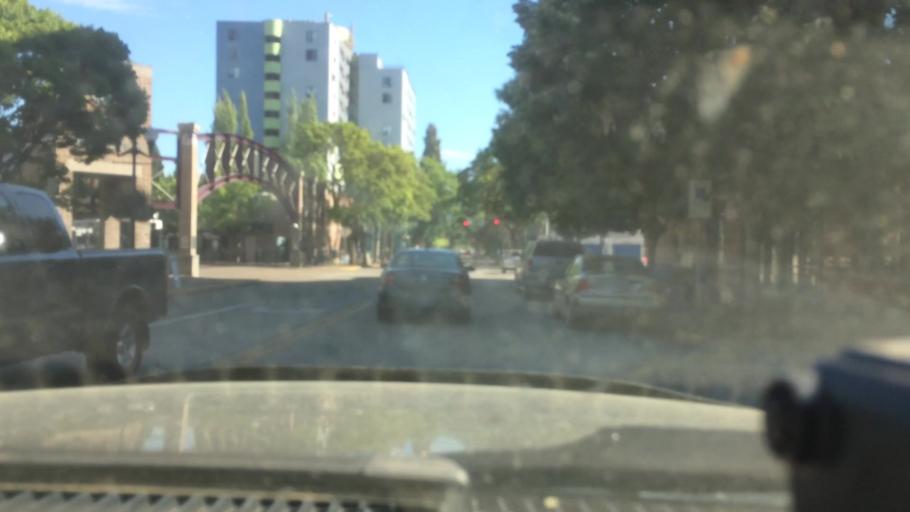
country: US
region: Oregon
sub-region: Lane County
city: Eugene
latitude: 44.0487
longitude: -123.0943
